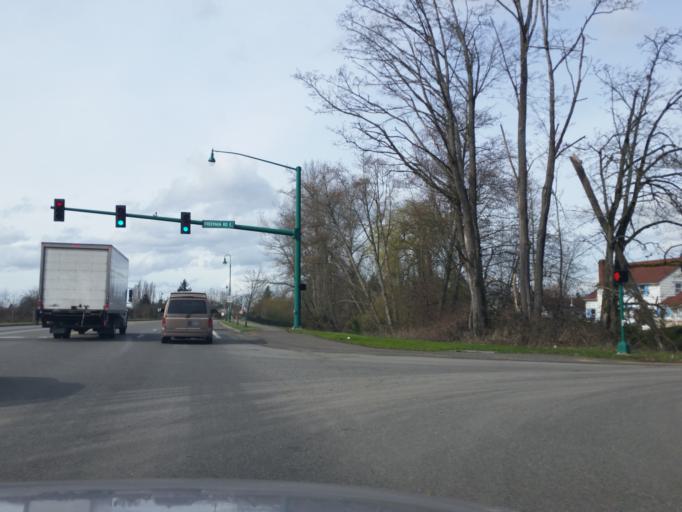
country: US
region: Washington
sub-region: Pierce County
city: Milton
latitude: 47.2206
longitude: -122.3205
